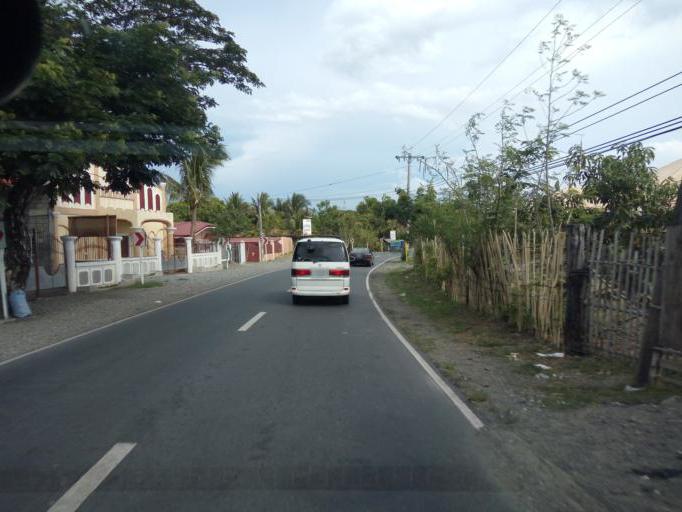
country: PH
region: Central Luzon
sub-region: Province of Nueva Ecija
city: Sibul
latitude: 15.7999
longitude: 120.9737
